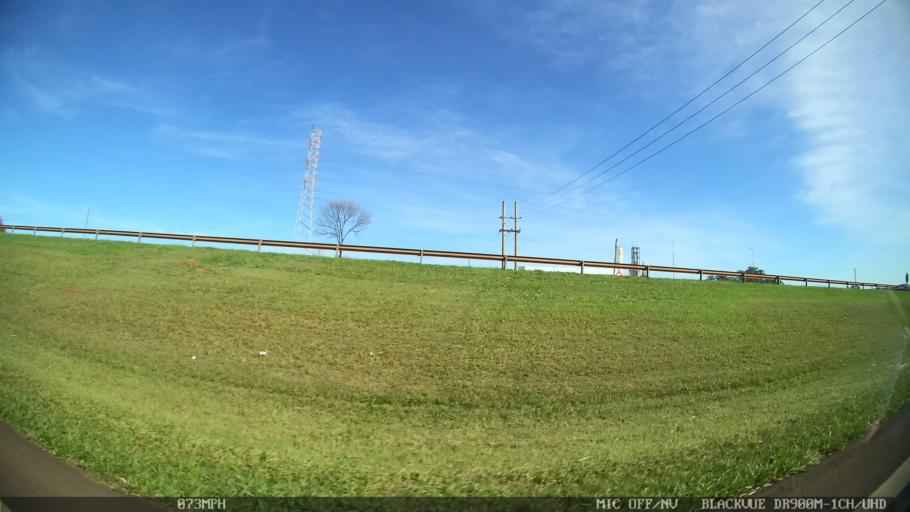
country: BR
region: Sao Paulo
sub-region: Araras
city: Araras
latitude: -22.2967
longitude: -47.3925
